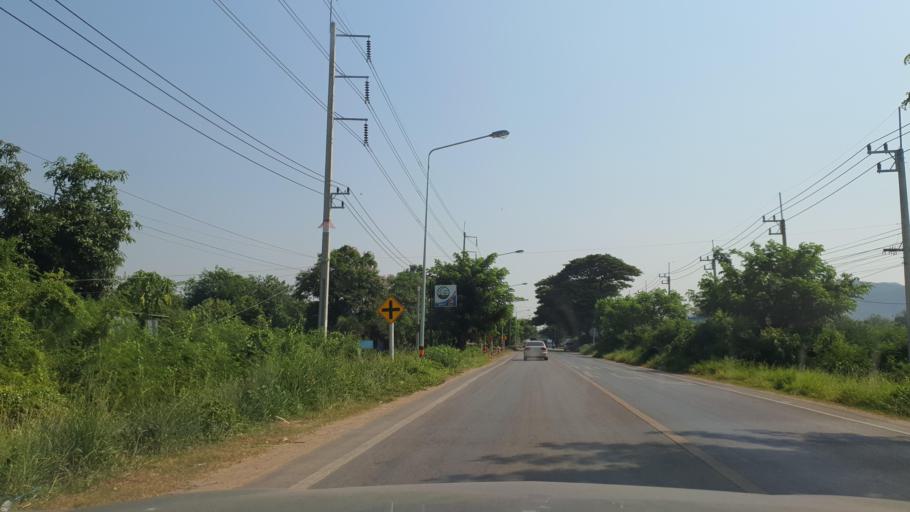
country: TH
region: Kanchanaburi
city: Kanchanaburi
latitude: 14.0569
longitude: 99.4760
